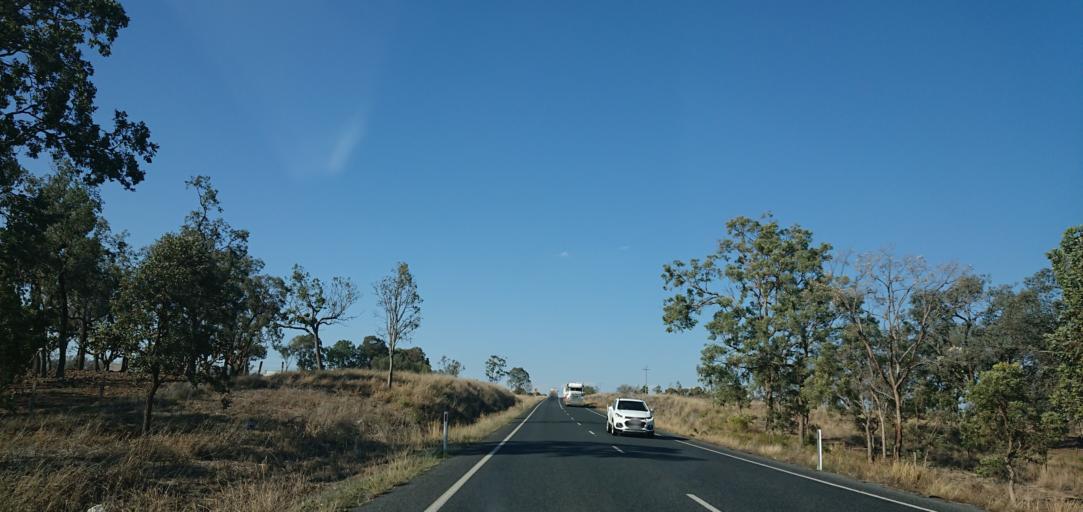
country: AU
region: Queensland
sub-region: Toowoomba
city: Westbrook
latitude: -27.6468
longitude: 151.7284
